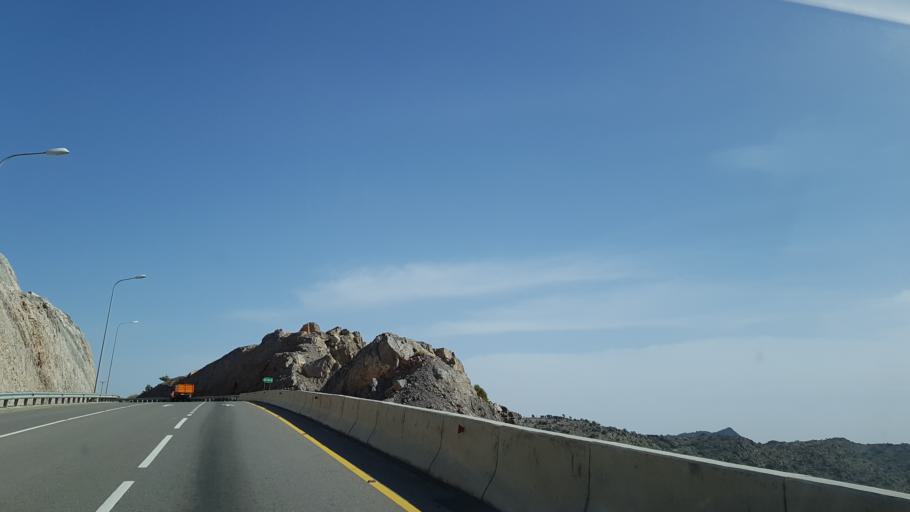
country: OM
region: Muhafazat ad Dakhiliyah
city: Izki
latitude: 23.0600
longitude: 57.7268
